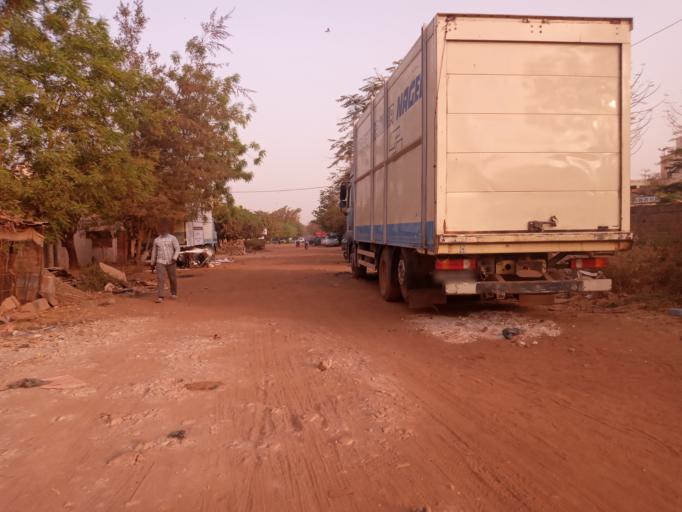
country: ML
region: Bamako
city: Bamako
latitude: 12.5871
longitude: -7.9539
